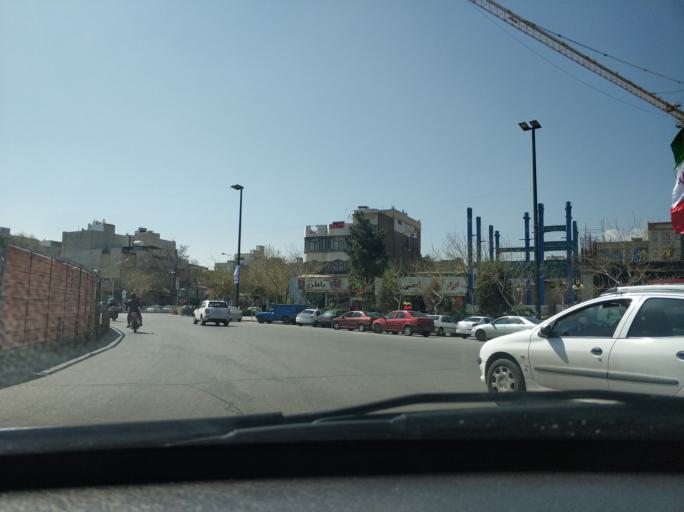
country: IR
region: Razavi Khorasan
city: Mashhad
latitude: 36.2682
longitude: 59.5982
